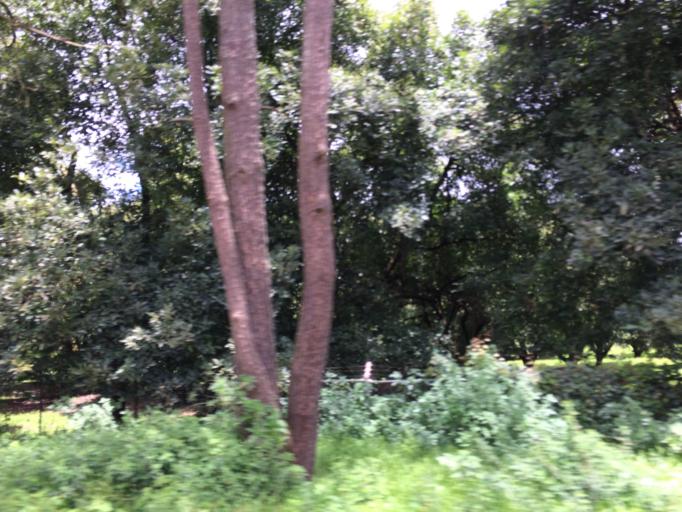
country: MX
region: Michoacan
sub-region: Uruapan
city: Santa Ana Zirosto
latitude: 19.5514
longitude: -102.3127
